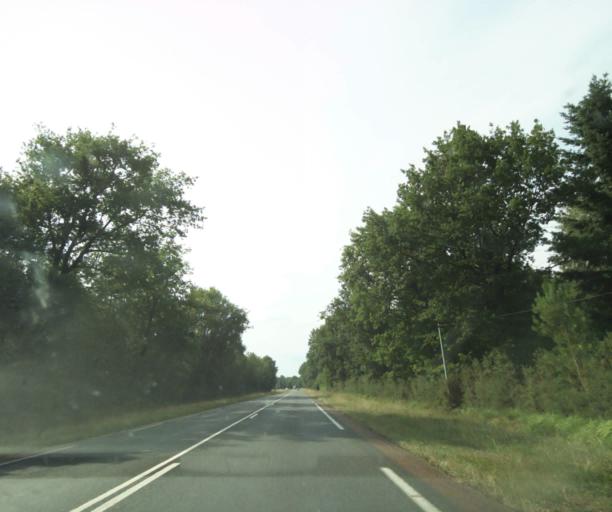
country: FR
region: Pays de la Loire
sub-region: Departement de la Sarthe
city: Marigne-Laille
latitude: 47.7997
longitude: 0.3282
